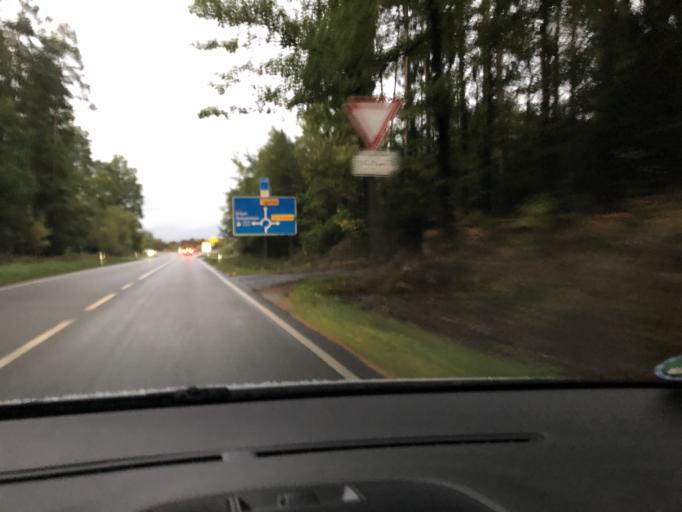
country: DE
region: Thuringia
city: Langewiesen
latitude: 50.7014
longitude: 10.9610
